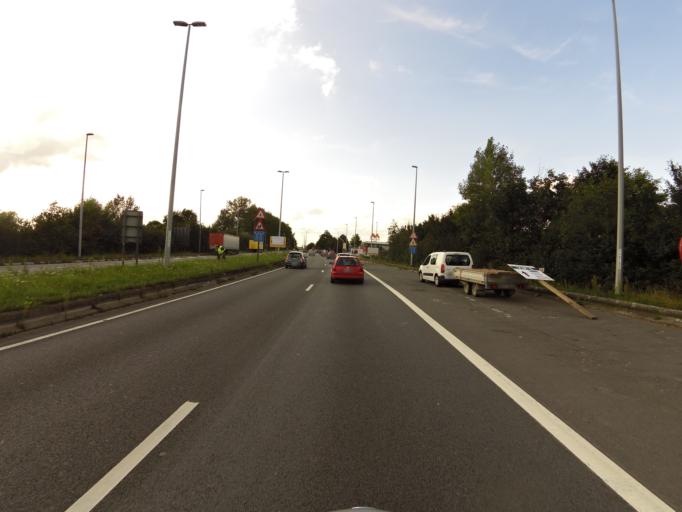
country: BE
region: Flanders
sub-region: Provincie West-Vlaanderen
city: Waregem
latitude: 50.8725
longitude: 3.4416
